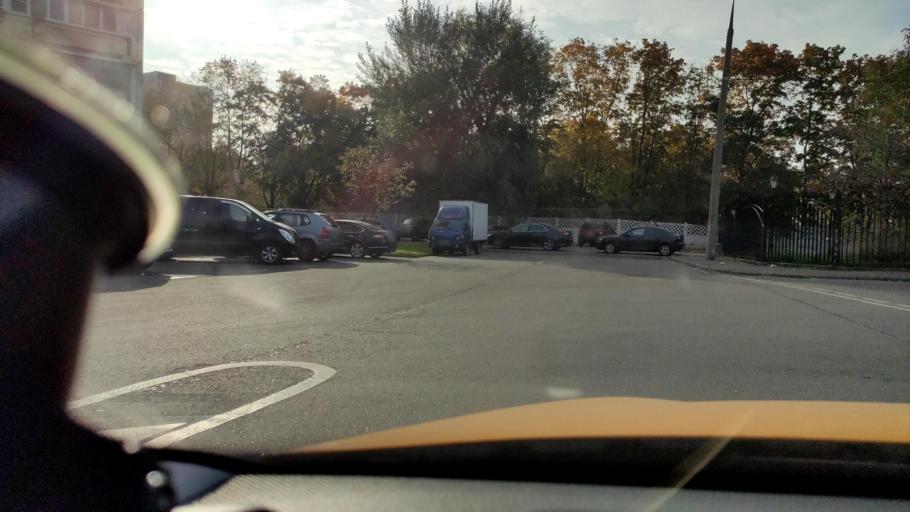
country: RU
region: Moscow
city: Mar'ino
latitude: 55.6759
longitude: 37.7165
